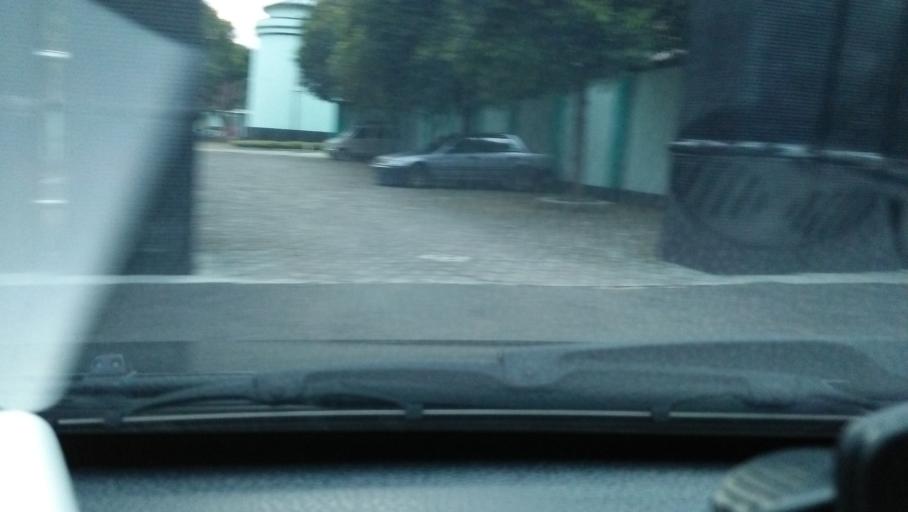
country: ID
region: Central Java
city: Magelang
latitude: -7.4661
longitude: 110.2256
